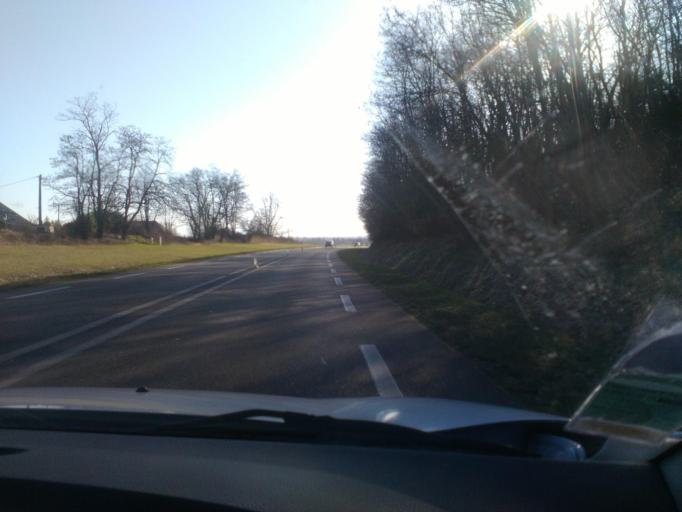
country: FR
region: Alsace
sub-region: Departement du Bas-Rhin
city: Mutzig
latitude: 48.5287
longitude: 7.4589
